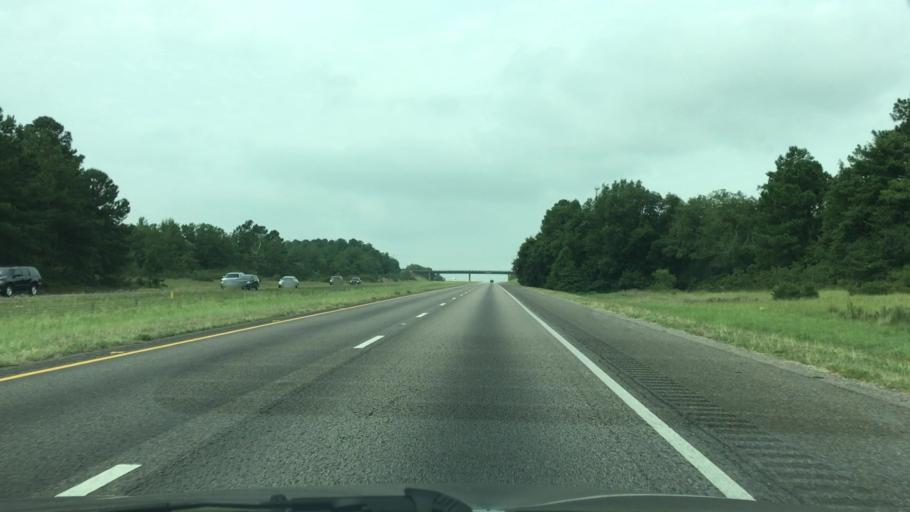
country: US
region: South Carolina
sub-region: Edgefield County
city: Murphys Estates
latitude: 33.5955
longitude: -81.8729
